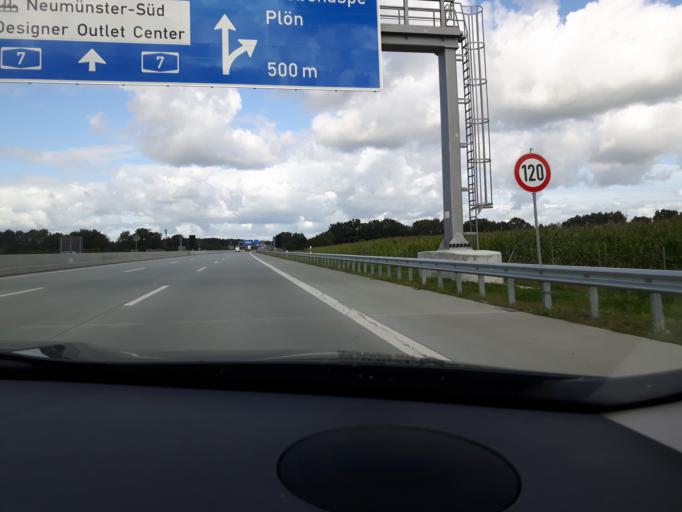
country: DE
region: Schleswig-Holstein
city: Grossenaspe
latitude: 53.9946
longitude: 9.9373
